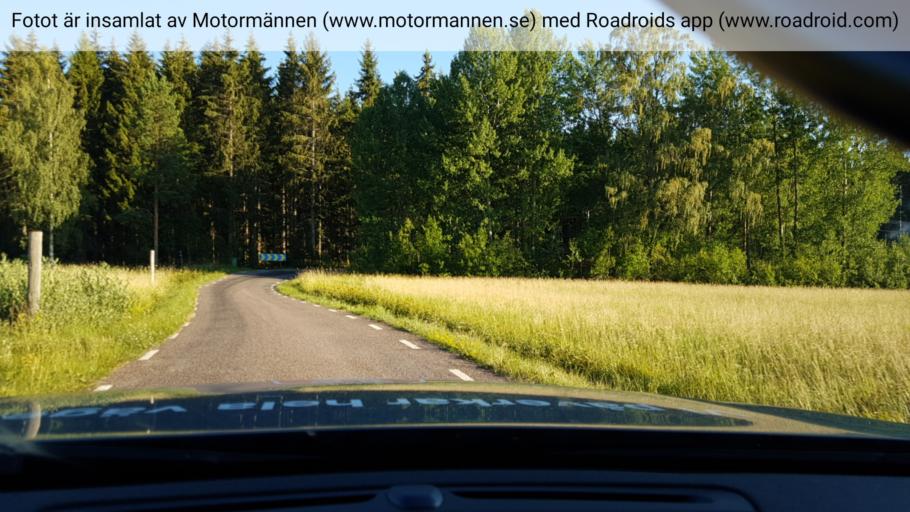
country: SE
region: Vaestmanland
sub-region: Surahammars Kommun
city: Surahammar
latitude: 59.6765
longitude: 16.0817
